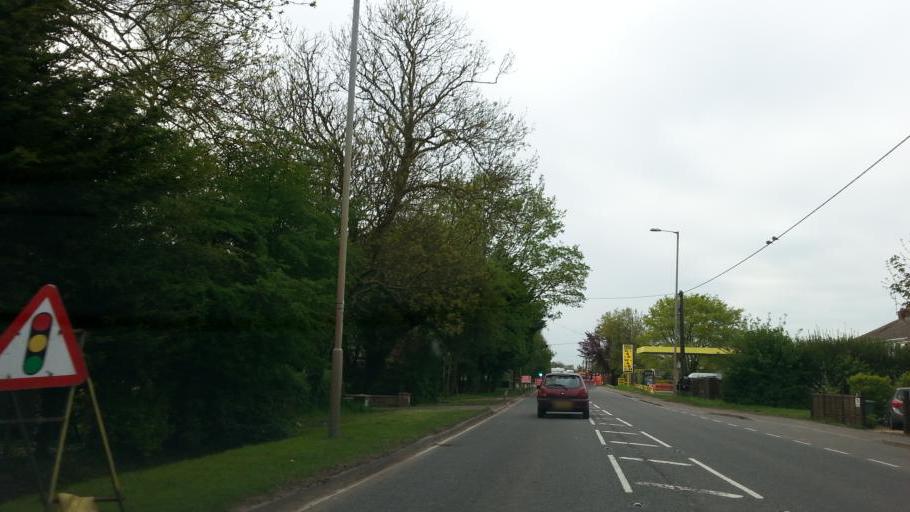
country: GB
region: England
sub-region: Cambridgeshire
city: March
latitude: 52.5687
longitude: 0.0605
